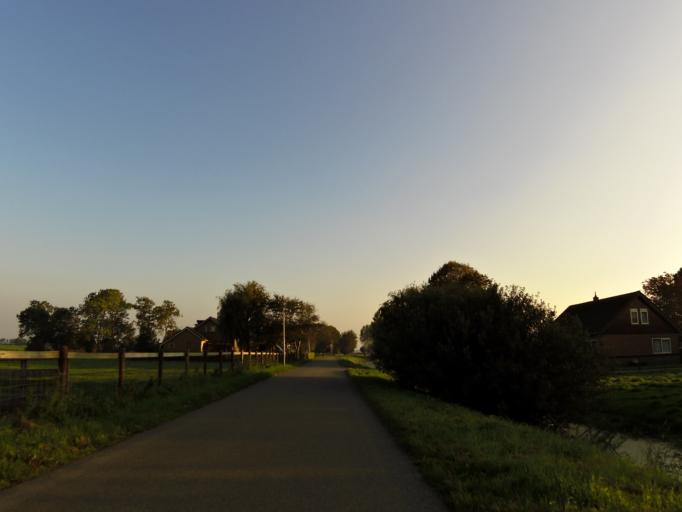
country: NL
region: South Holland
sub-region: Gemeente Leiderdorp
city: Leiderdorp
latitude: 52.1602
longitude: 4.5865
